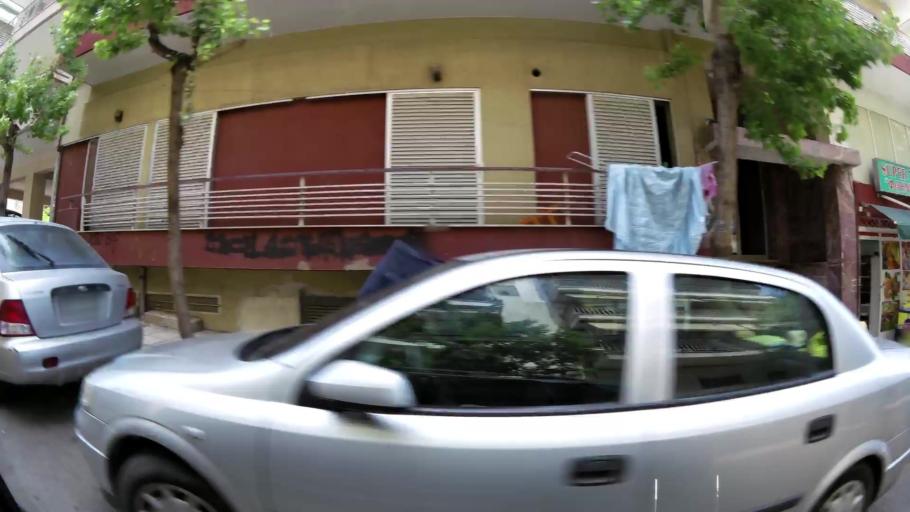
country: GR
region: Central Macedonia
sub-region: Nomos Thessalonikis
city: Triandria
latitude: 40.6170
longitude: 22.9793
